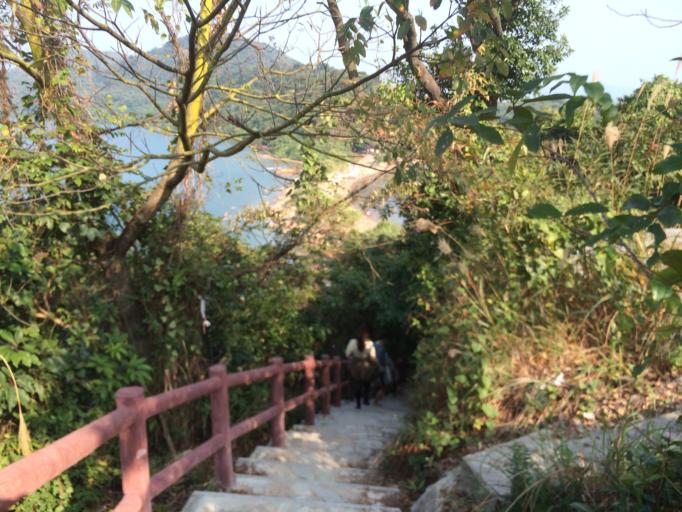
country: HK
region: Tai Po
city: Tai Po
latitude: 22.4500
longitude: 114.2214
